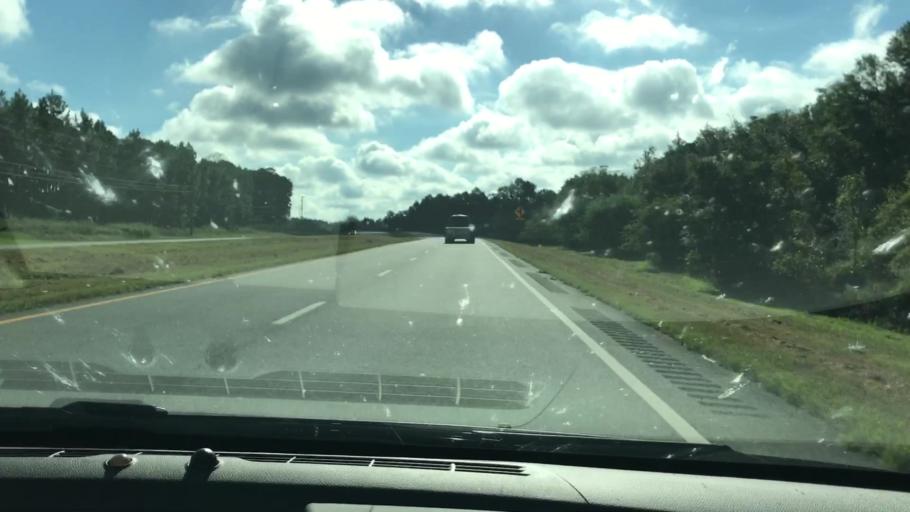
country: US
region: Georgia
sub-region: Worth County
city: Sylvester
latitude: 31.5507
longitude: -83.9700
